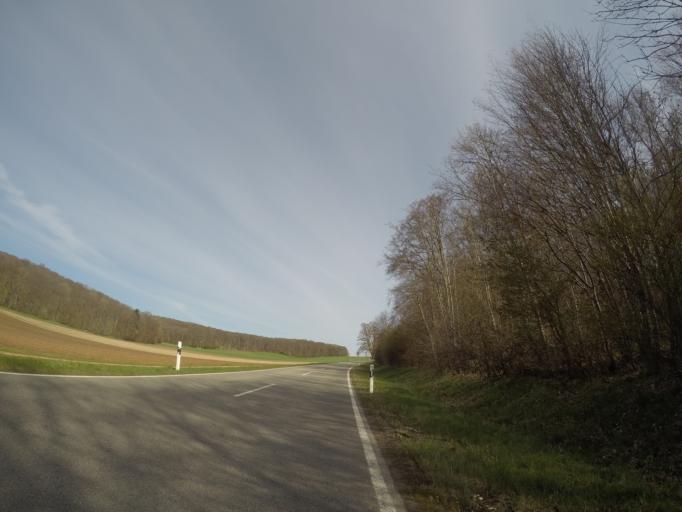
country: DE
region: Baden-Wuerttemberg
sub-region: Regierungsbezirk Stuttgart
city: Hohenstadt
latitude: 48.5295
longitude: 9.6535
